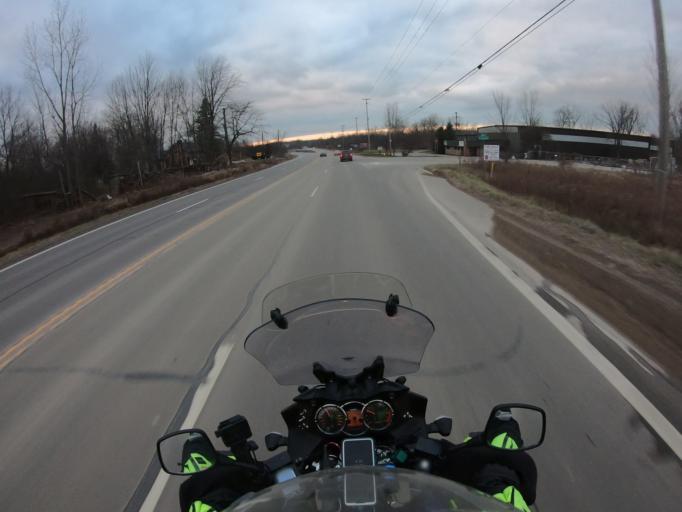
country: US
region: Michigan
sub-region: Genesee County
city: Grand Blanc
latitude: 42.8658
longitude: -83.5856
